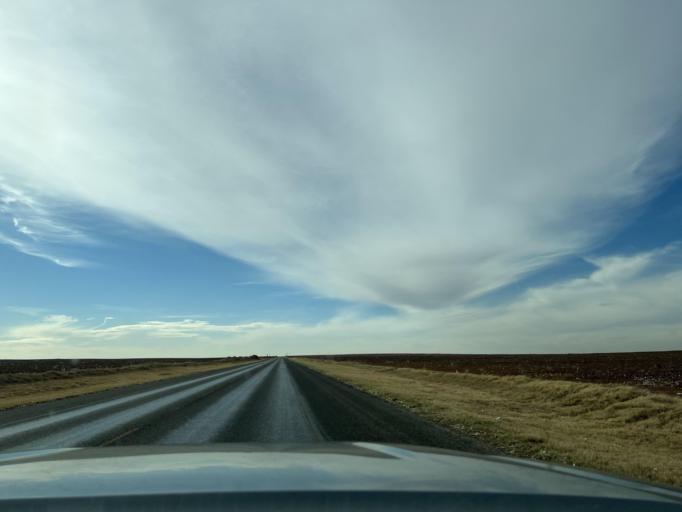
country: US
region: Texas
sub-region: Fisher County
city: Roby
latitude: 32.7419
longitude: -100.4412
